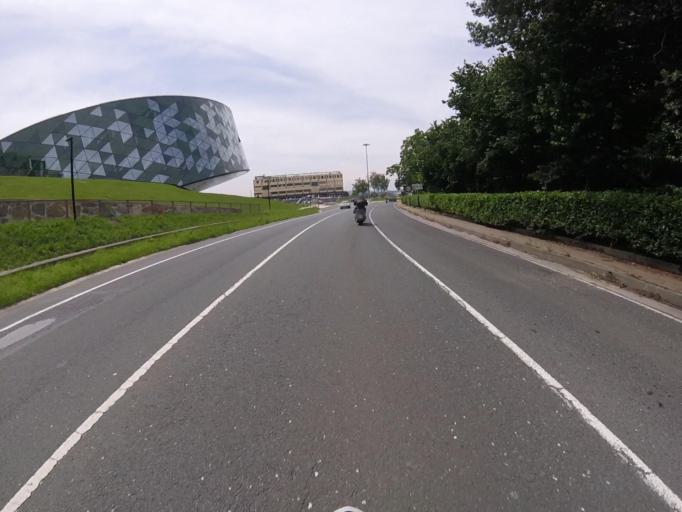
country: ES
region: Basque Country
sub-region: Provincia de Guipuzcoa
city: Hernani
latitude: 43.2767
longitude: -1.9858
